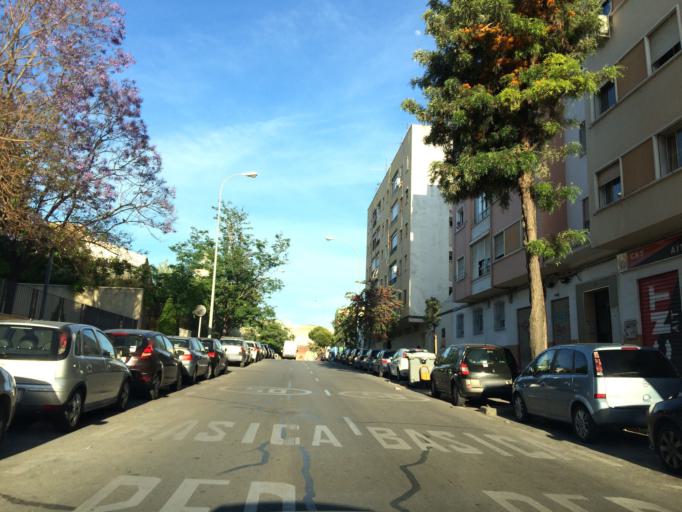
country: ES
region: Andalusia
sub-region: Provincia de Malaga
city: Malaga
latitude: 36.7258
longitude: -4.4342
